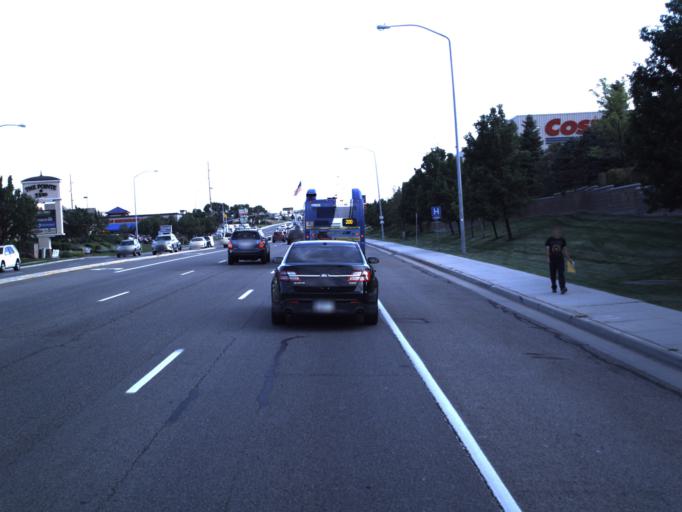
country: US
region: Utah
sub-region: Salt Lake County
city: Murray
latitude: 40.6588
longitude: -111.8884
